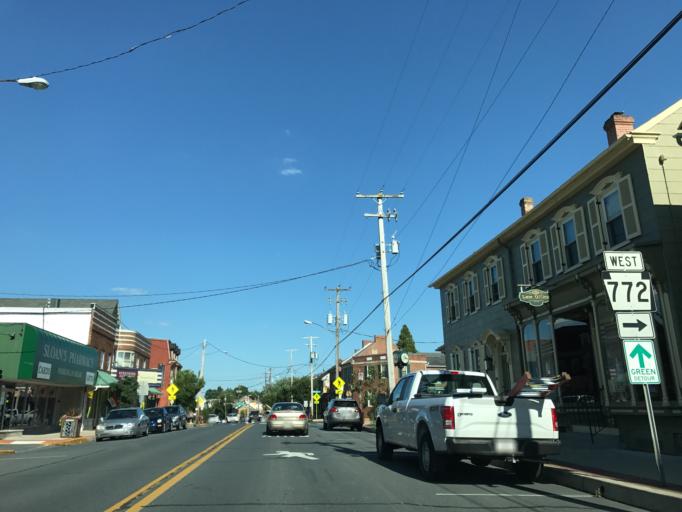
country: US
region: Pennsylvania
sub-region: Lancaster County
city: Mount Joy
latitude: 40.1095
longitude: -76.5010
